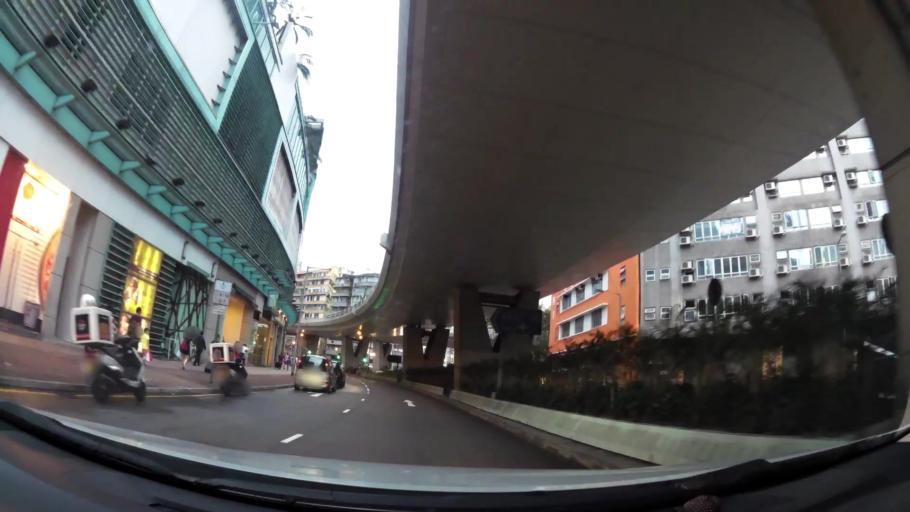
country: HK
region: Sham Shui Po
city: Sham Shui Po
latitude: 22.3239
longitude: 114.1620
